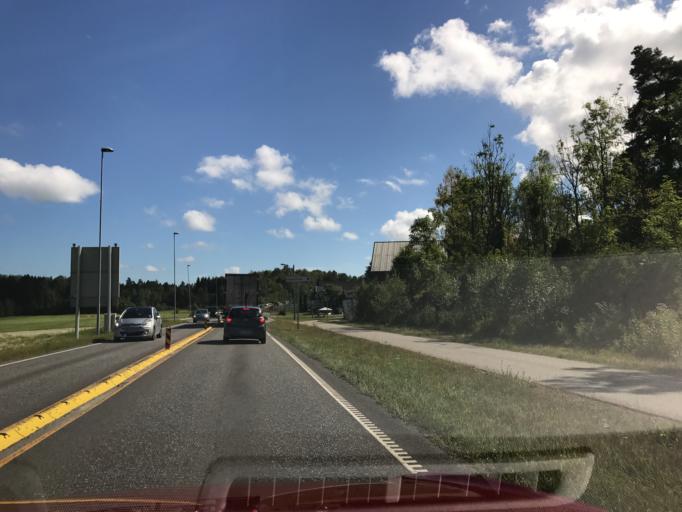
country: NO
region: Telemark
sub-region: Bamble
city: Langesund
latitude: 59.0307
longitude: 9.6787
